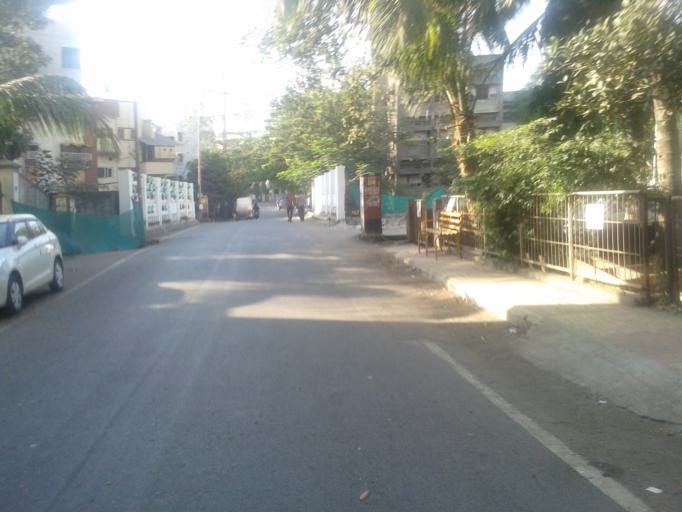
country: IN
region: Maharashtra
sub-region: Thane
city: Dombivli
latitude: 19.2054
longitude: 73.0906
